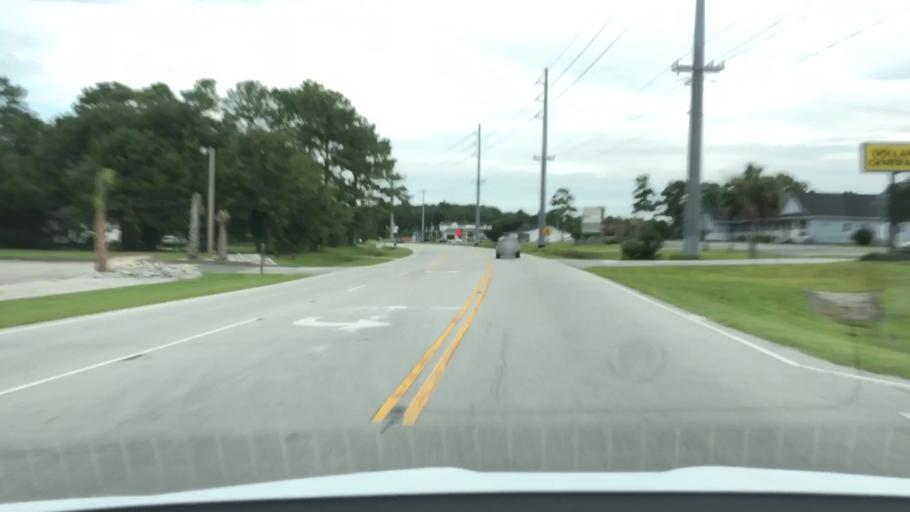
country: US
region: North Carolina
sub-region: Carteret County
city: Cape Carteret
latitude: 34.7140
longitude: -77.0679
